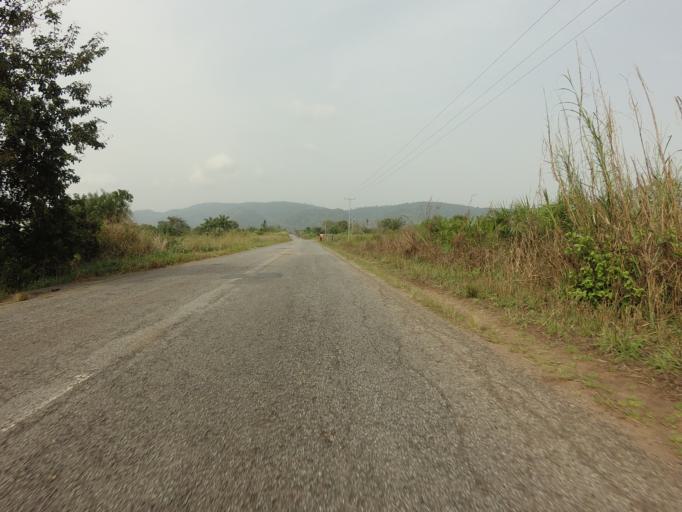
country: GH
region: Volta
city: Ho
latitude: 6.5755
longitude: 0.3286
